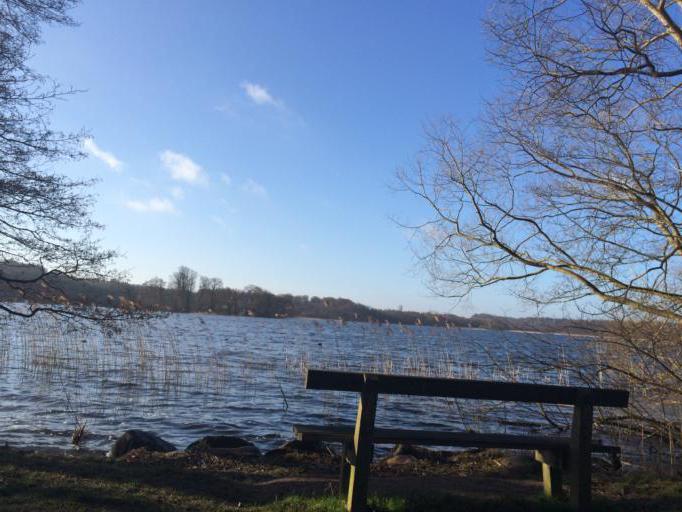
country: DK
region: Capital Region
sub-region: Fureso Kommune
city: Farum
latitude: 55.8072
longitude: 12.3724
